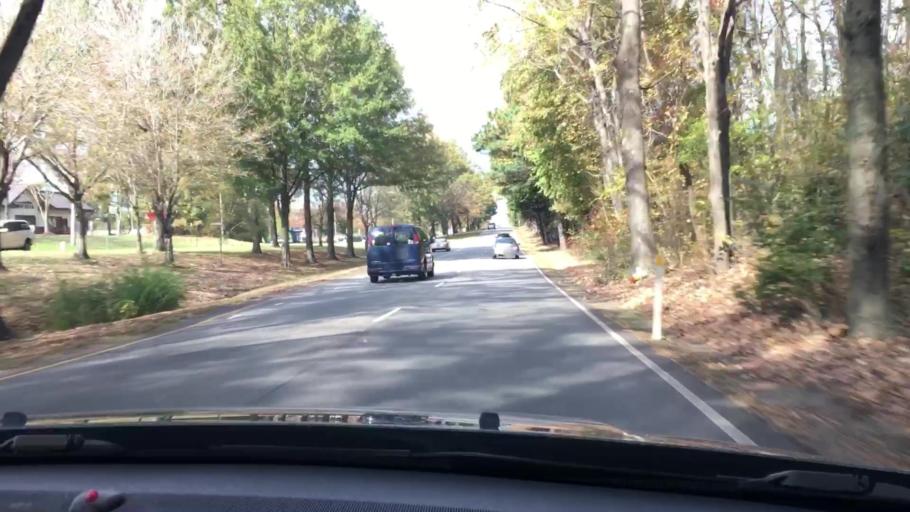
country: US
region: Virginia
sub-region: James City County
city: Williamsburg
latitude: 37.3043
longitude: -76.7283
